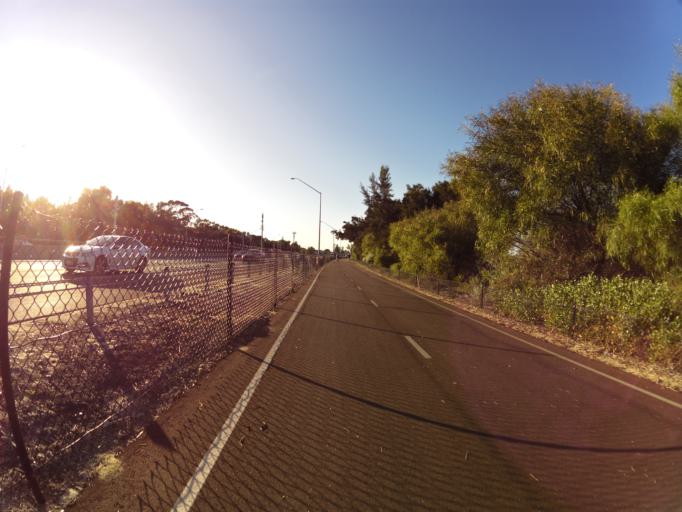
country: AU
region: Western Australia
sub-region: South Perth
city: Como
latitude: -31.9842
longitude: 115.8511
